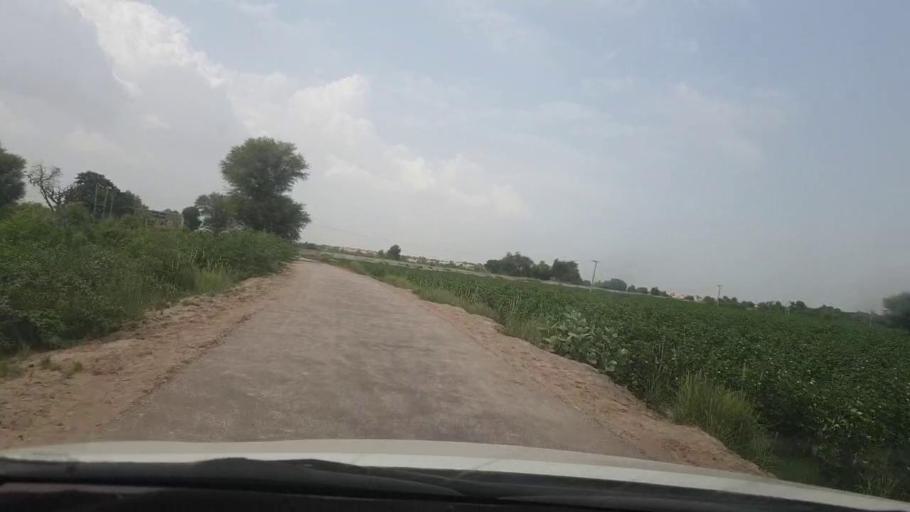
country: PK
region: Sindh
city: Kot Diji
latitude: 27.3101
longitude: 69.0121
